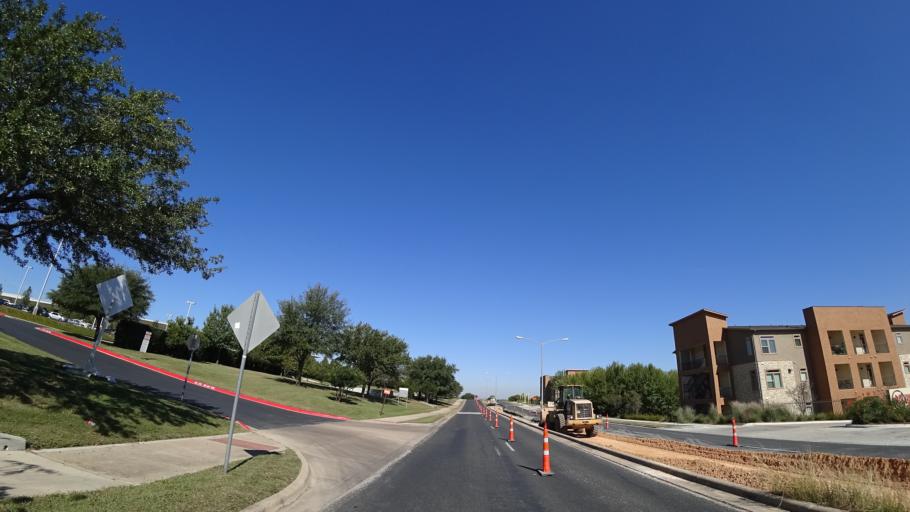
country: US
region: Texas
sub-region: Travis County
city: Austin
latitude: 30.2216
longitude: -97.7077
